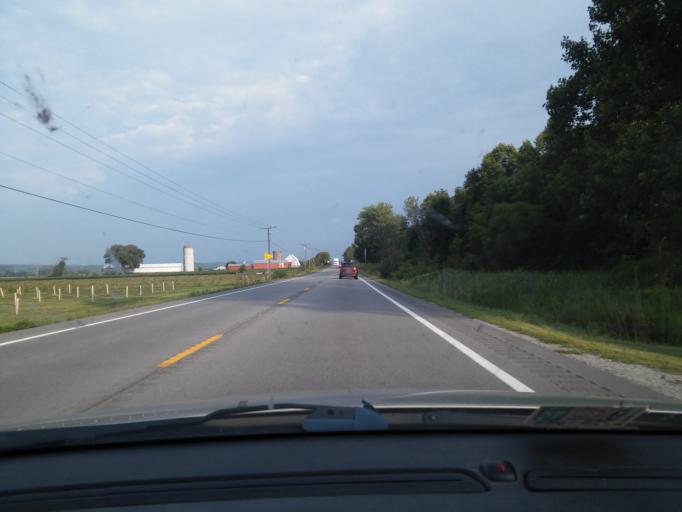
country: US
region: West Virginia
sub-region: Putnam County
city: Buffalo
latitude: 38.7603
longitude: -81.9965
